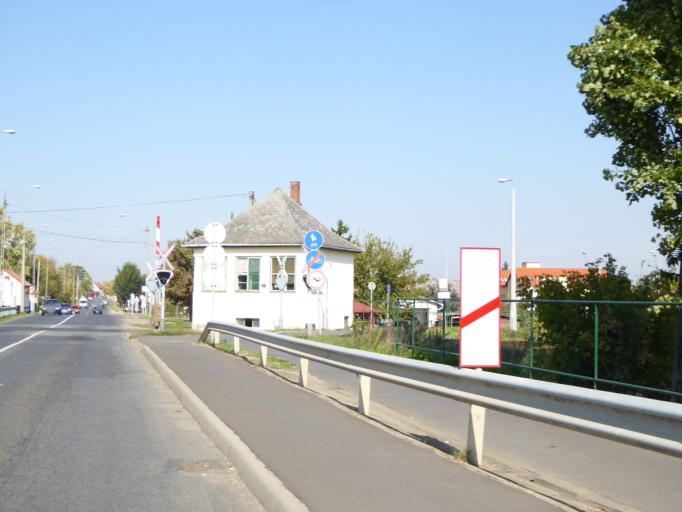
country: HU
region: Hajdu-Bihar
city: Berettyoujfalu
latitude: 47.2096
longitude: 21.5374
